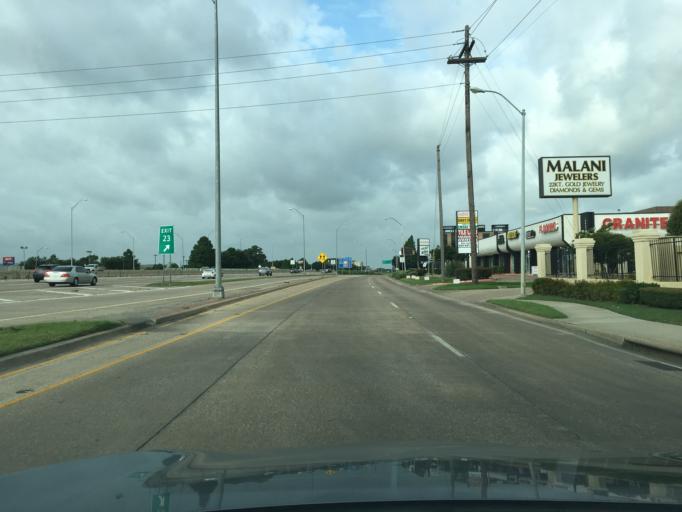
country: US
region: Texas
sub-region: Dallas County
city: Richardson
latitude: 32.9478
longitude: -96.7371
